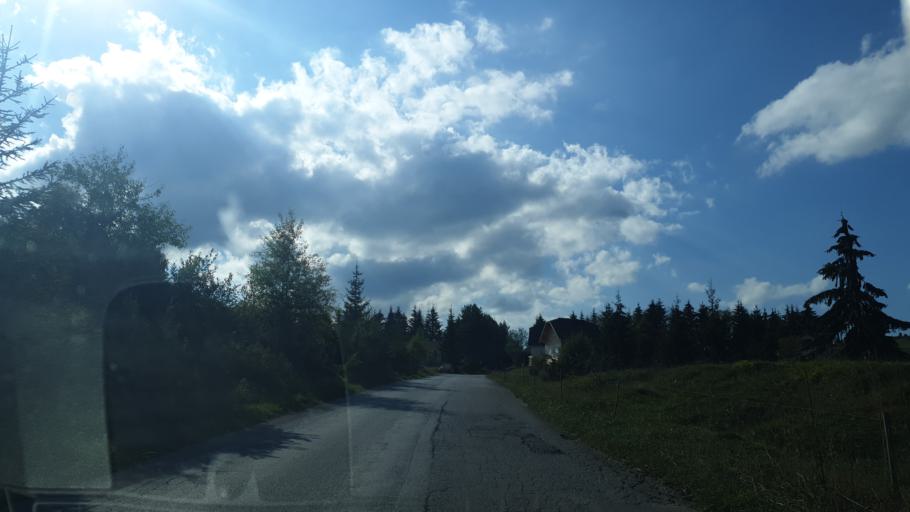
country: RS
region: Central Serbia
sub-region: Zlatiborski Okrug
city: Nova Varos
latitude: 43.4253
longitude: 19.9136
